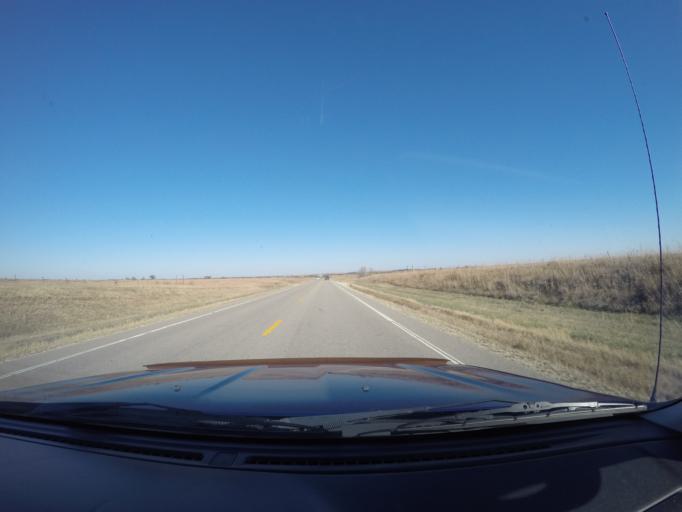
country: US
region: Kansas
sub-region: Riley County
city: Ogden
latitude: 39.3081
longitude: -96.7557
